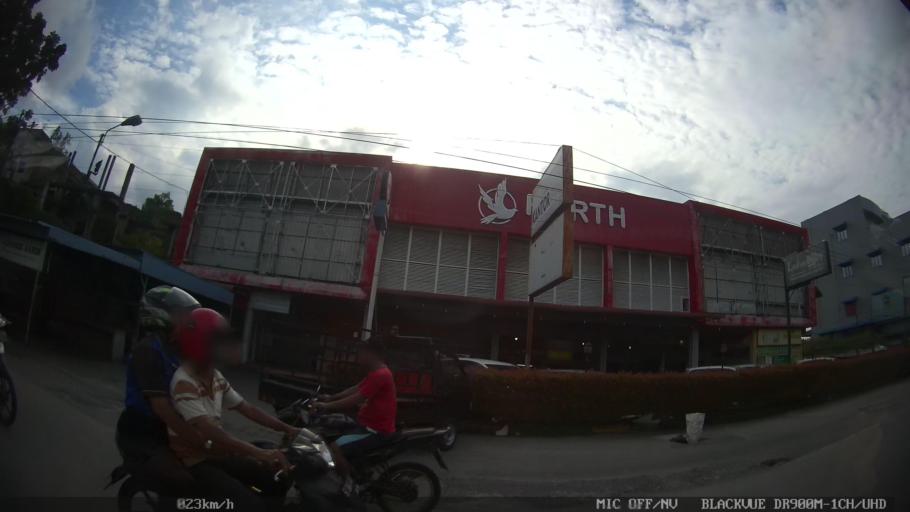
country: ID
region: North Sumatra
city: Medan
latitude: 3.6185
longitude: 98.6807
